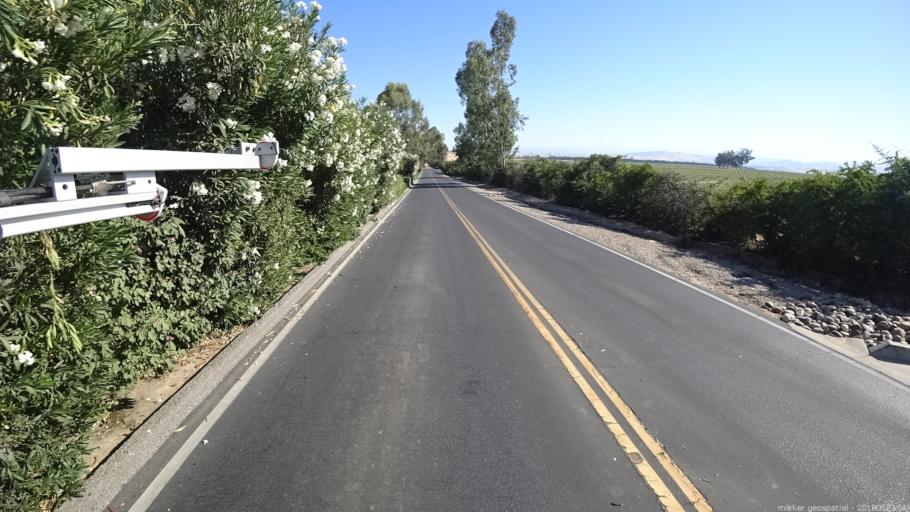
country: US
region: California
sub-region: Madera County
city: Bonadelle Ranchos-Madera Ranchos
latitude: 36.9598
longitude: -119.7573
